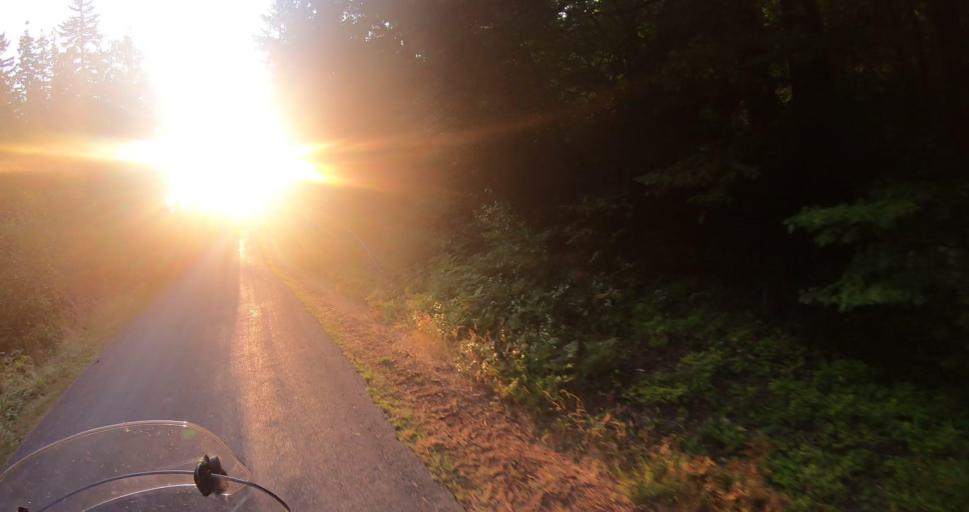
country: US
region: Oregon
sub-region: Hood River County
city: Odell
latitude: 45.4655
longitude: -121.6230
